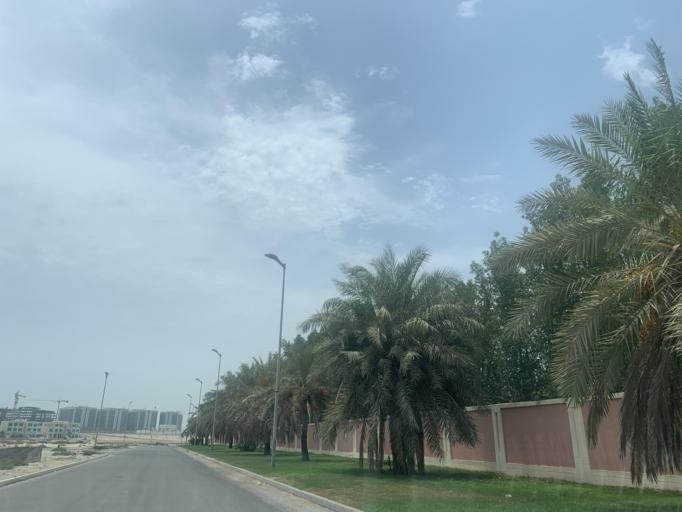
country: BH
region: Muharraq
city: Al Hadd
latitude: 26.2772
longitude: 50.6678
